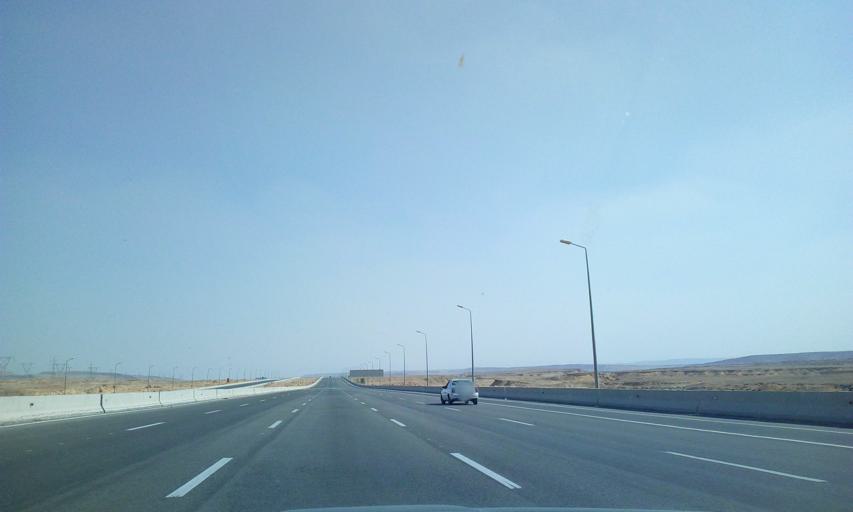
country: EG
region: As Suways
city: Ain Sukhna
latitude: 29.8440
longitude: 31.8755
